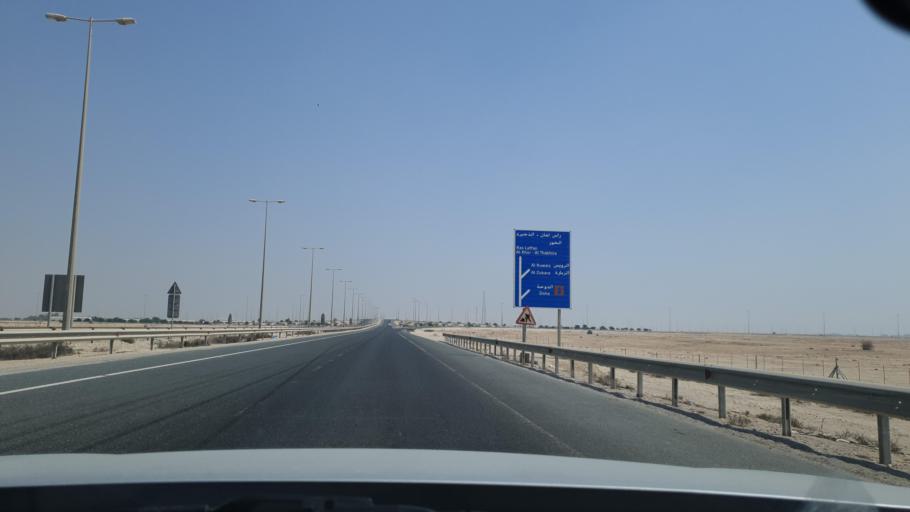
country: QA
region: Baladiyat az Za`ayin
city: Az Za`ayin
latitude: 25.6201
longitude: 51.3934
